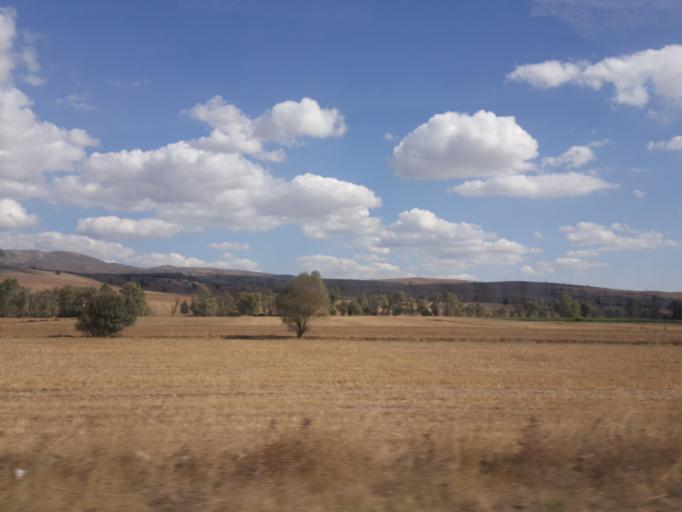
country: TR
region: Tokat
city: Camlibel
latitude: 40.1876
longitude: 36.4546
